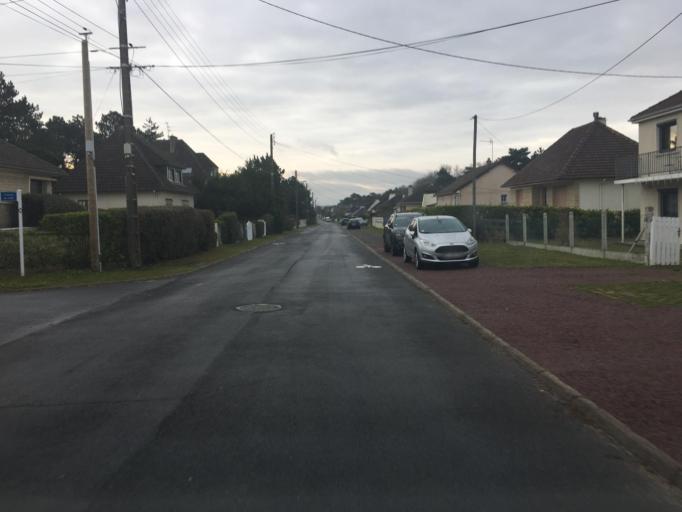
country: FR
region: Lower Normandy
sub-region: Departement du Calvados
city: Merville-Franceville-Plage
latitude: 49.2837
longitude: -0.2106
